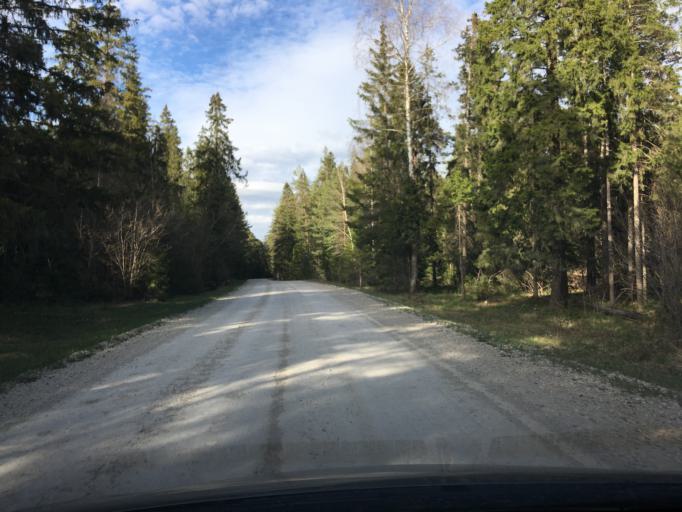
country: EE
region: Raplamaa
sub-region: Maerjamaa vald
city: Marjamaa
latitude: 59.0211
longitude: 24.4352
